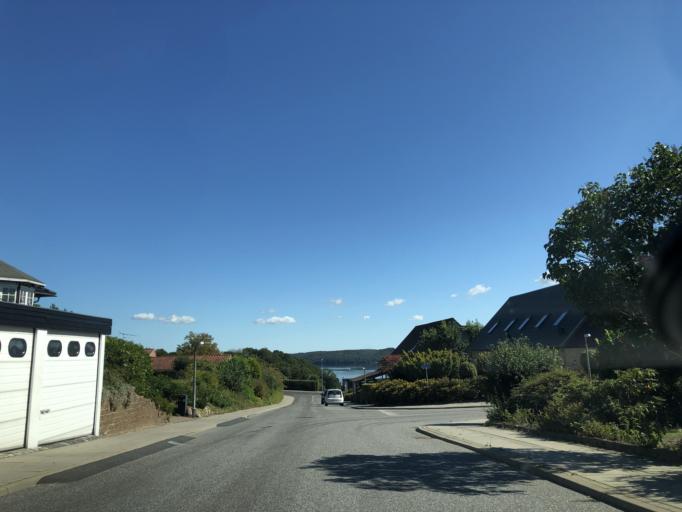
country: DK
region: North Denmark
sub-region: Mariagerfjord Kommune
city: Hobro
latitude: 56.6441
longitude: 9.8033
